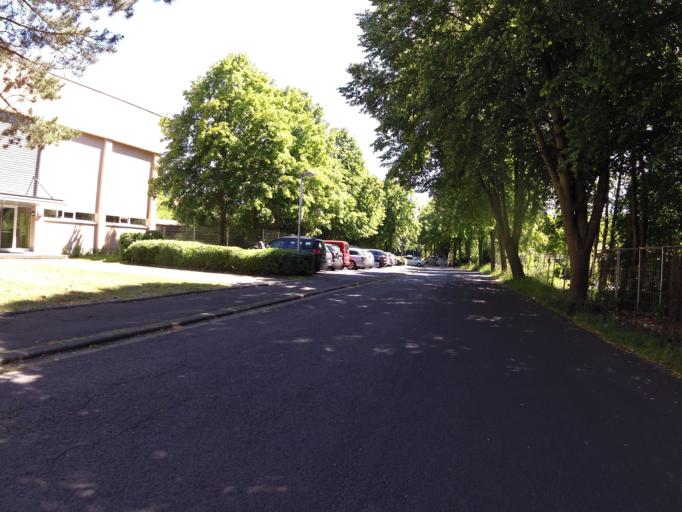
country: DE
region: Thuringia
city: Dankmarshausen
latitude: 50.9473
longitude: 10.0221
